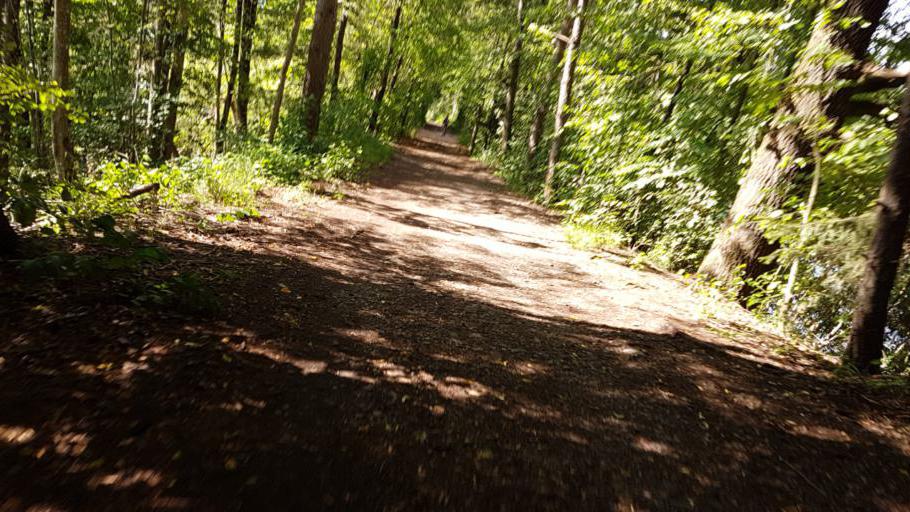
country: CH
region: Bern
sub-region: Bern-Mittelland District
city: Muri
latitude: 46.9147
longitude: 7.5039
